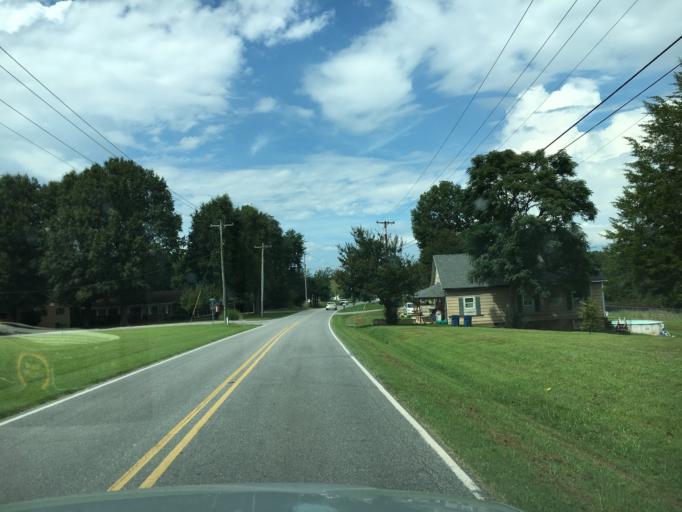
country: US
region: North Carolina
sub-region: Catawba County
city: Maiden
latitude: 35.5723
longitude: -81.1956
